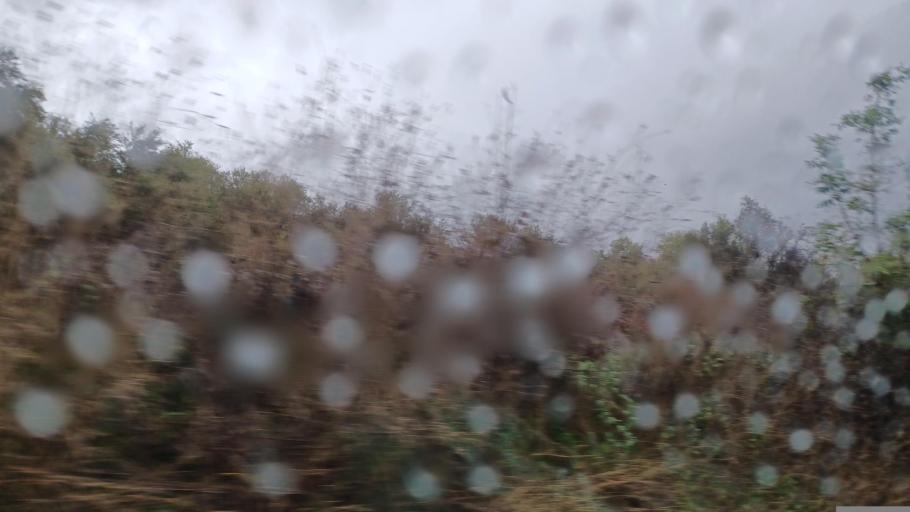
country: CY
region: Pafos
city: Mesogi
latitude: 34.8651
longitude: 32.5427
